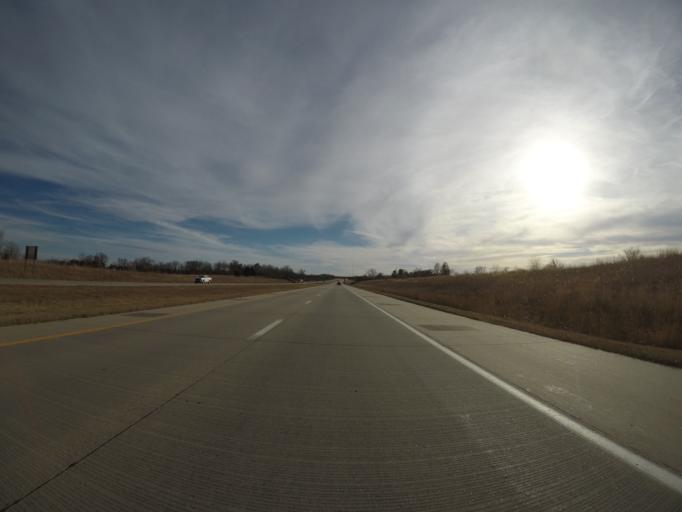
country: US
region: Kansas
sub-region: Franklin County
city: Ottawa
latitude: 38.6112
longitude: -95.2327
